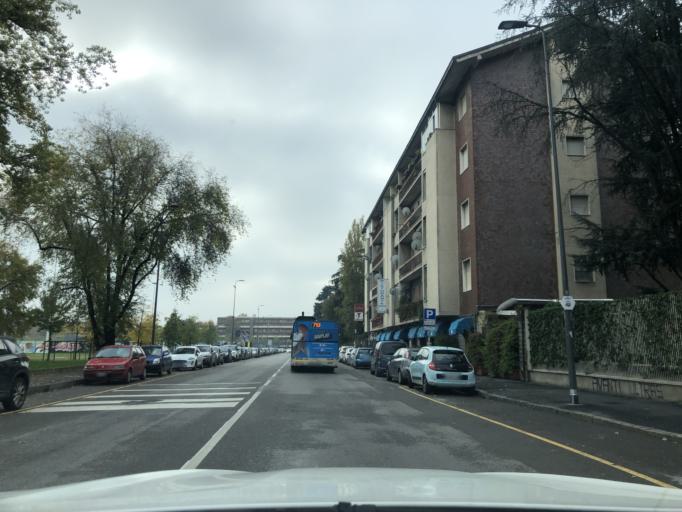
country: IT
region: Lombardy
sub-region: Citta metropolitana di Milano
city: Figino
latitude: 45.4793
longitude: 9.1174
